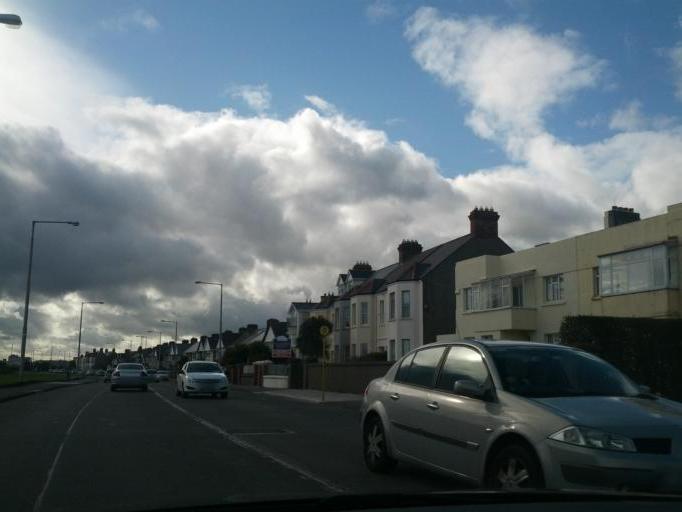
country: IE
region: Leinster
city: Dollymount
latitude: 53.3599
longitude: -6.1850
